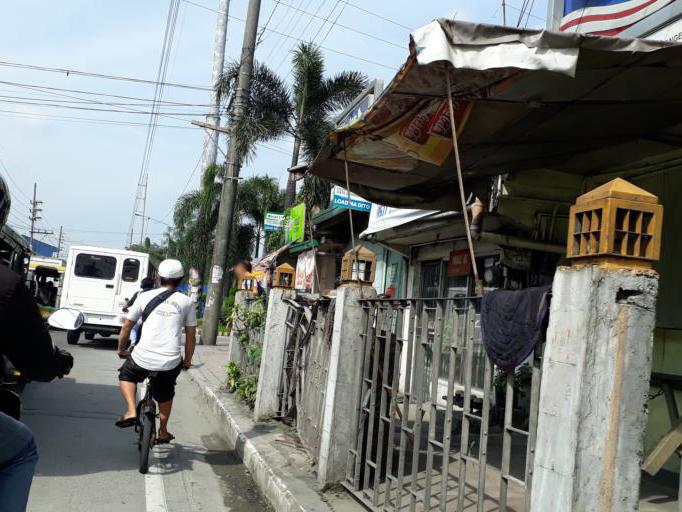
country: PH
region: Calabarzon
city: Bagong Pagasa
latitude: 14.6828
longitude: 121.0211
